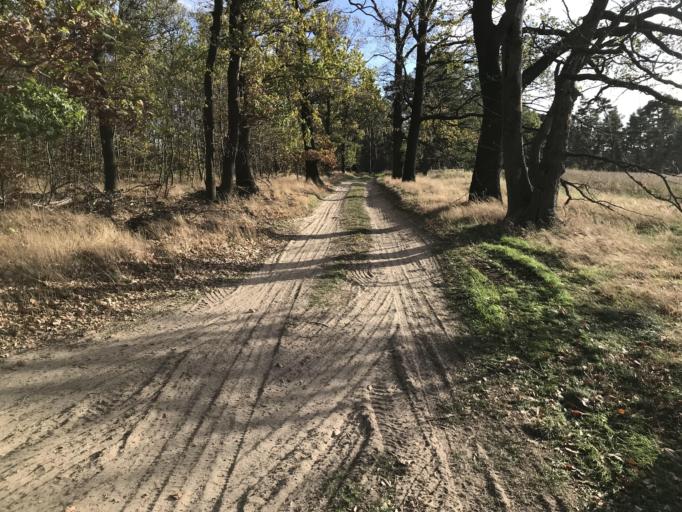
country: DE
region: Saxony-Anhalt
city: Derenburg
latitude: 51.8360
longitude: 10.9303
